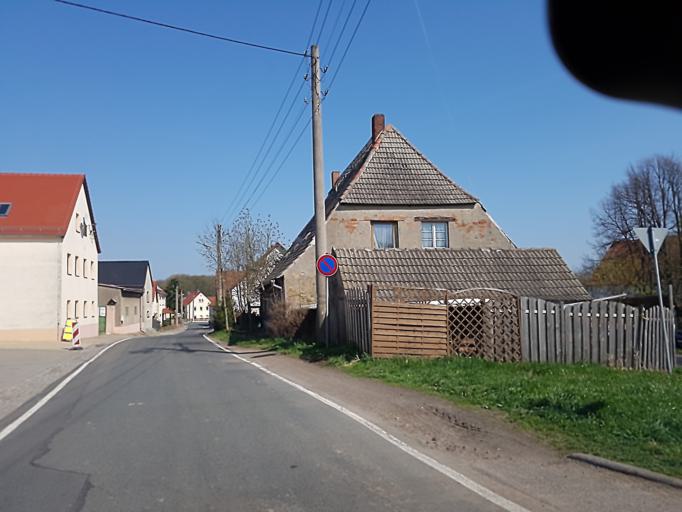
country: DE
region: Saxony
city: Cavertitz
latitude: 51.3862
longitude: 13.1253
